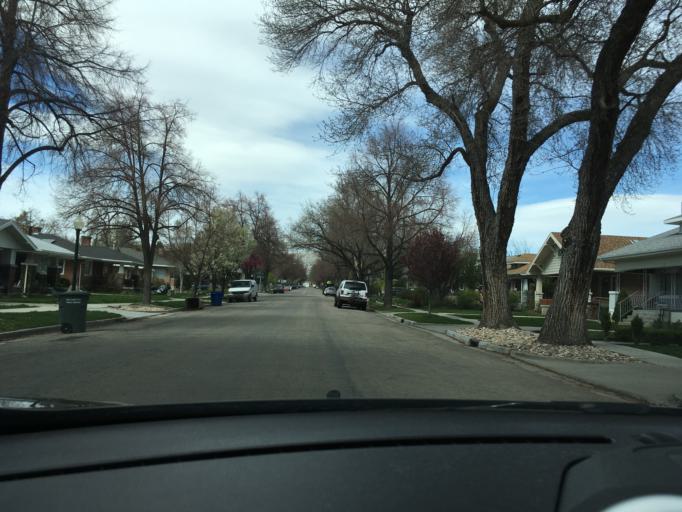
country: US
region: Utah
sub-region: Salt Lake County
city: South Salt Lake
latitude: 40.7382
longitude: -111.8625
